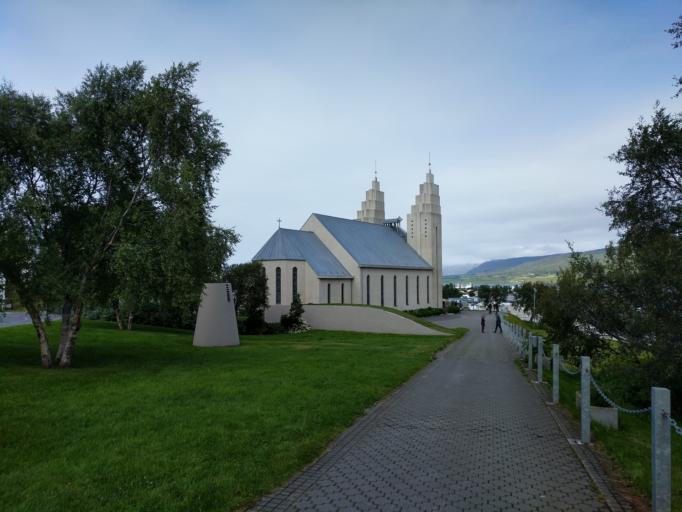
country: IS
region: Northeast
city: Akureyri
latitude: 65.6793
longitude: -18.0909
